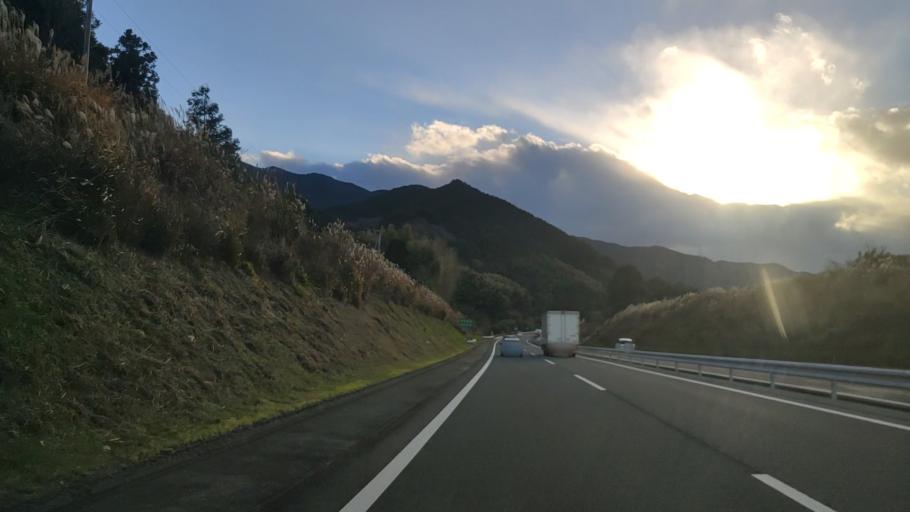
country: JP
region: Ehime
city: Saijo
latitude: 33.8682
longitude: 133.0589
